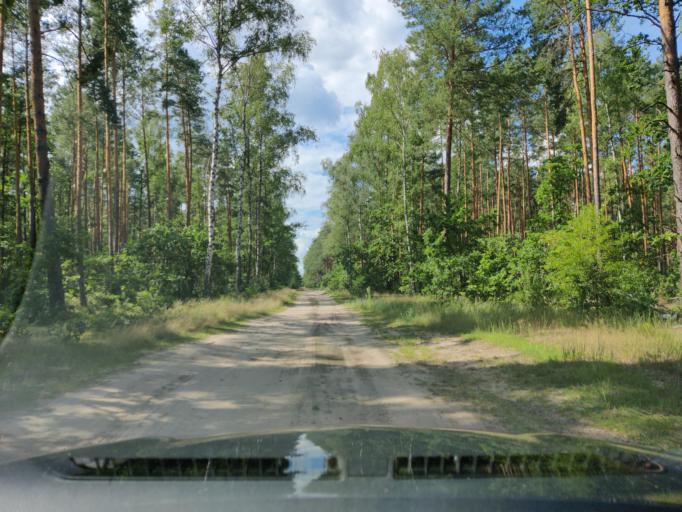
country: PL
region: Masovian Voivodeship
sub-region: Powiat pultuski
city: Obryte
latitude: 52.7399
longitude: 21.1680
